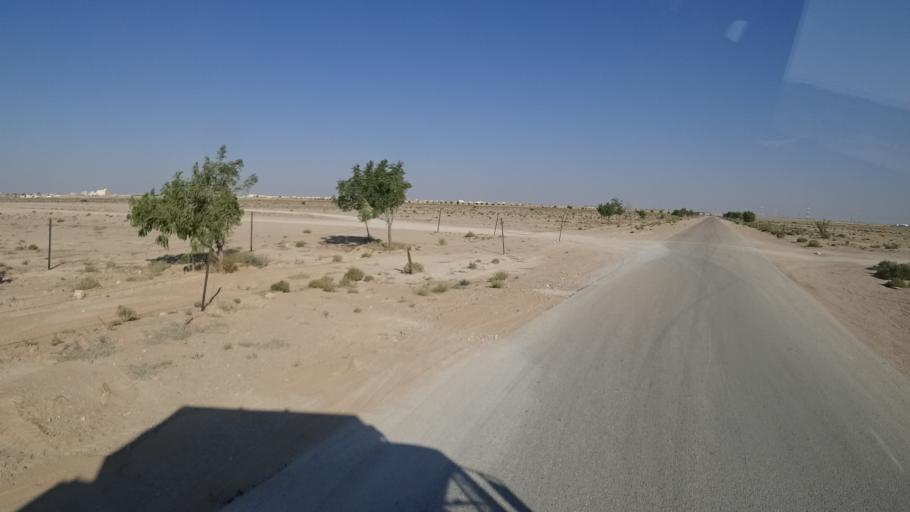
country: OM
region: Zufar
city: Salalah
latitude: 17.5960
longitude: 54.0269
